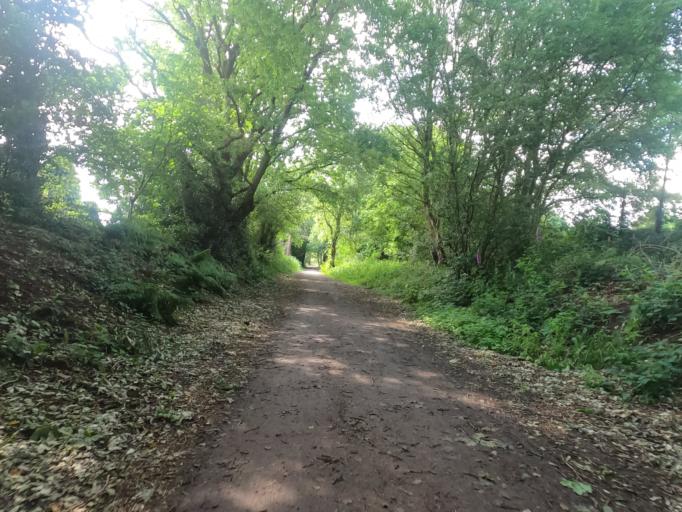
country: GB
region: England
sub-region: Cheshire West and Chester
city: Cuddington
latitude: 53.2101
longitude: -2.5855
